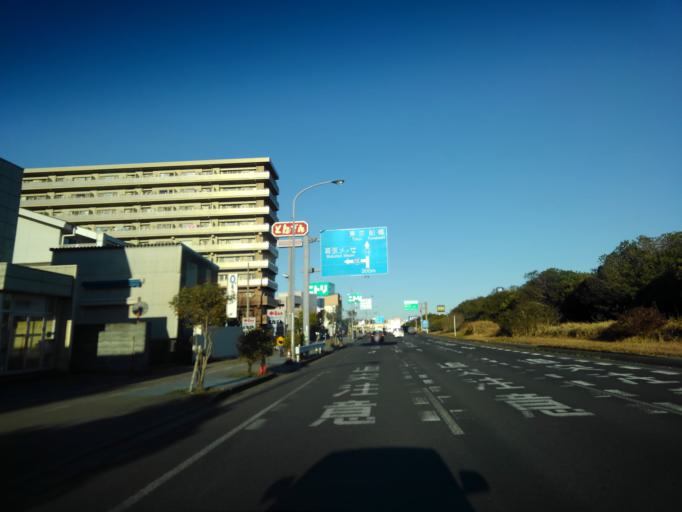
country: JP
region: Chiba
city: Funabashi
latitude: 35.6604
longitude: 140.0467
